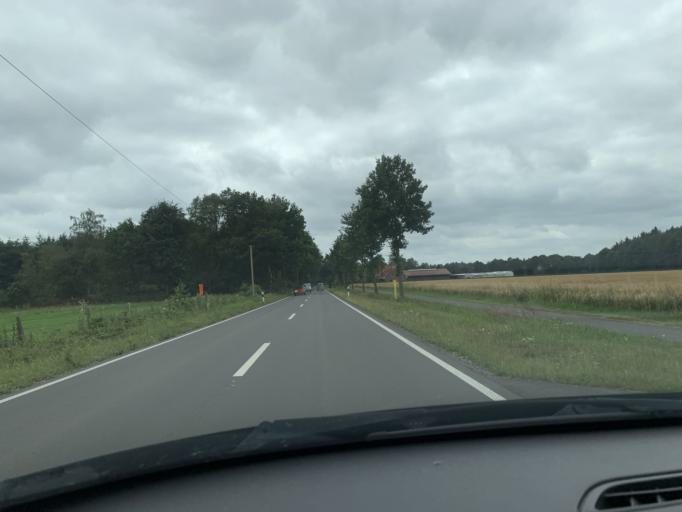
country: DE
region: Lower Saxony
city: Bad Zwischenahn
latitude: 53.2183
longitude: 7.9729
